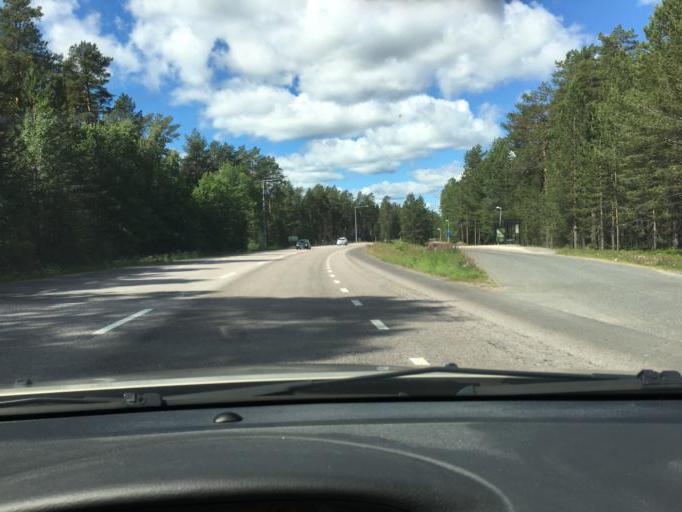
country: SE
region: Norrbotten
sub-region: Lulea Kommun
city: Bergnaset
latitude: 65.5775
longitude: 22.0884
